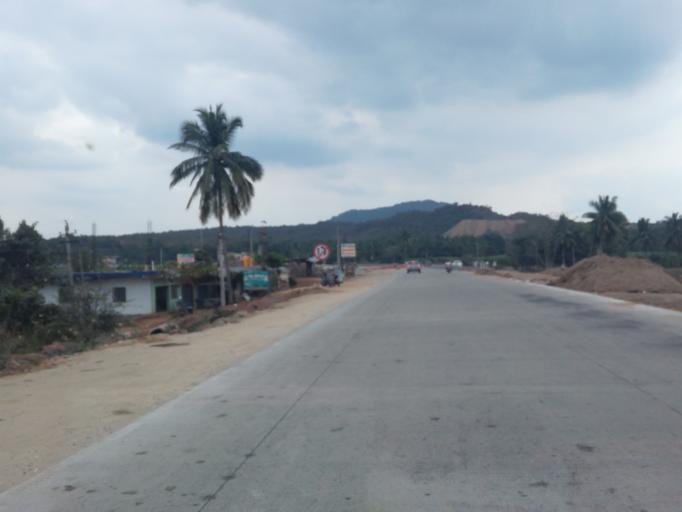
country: IN
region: Andhra Pradesh
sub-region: Chittoor
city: Ramapuram
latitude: 13.0993
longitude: 79.1252
